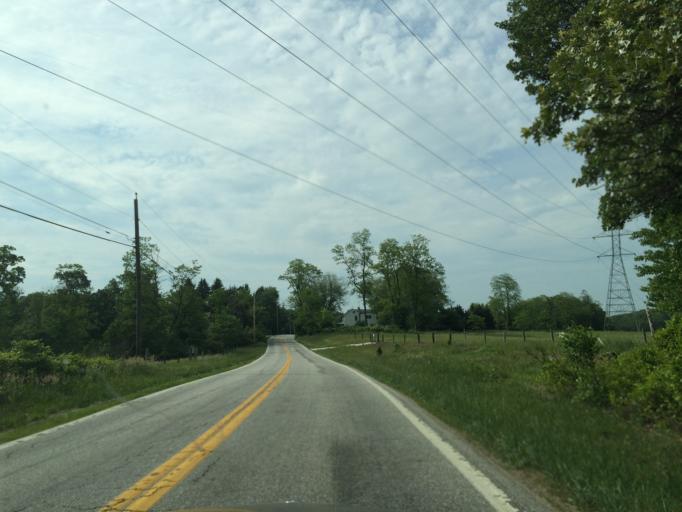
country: US
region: Maryland
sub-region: Baltimore County
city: Reisterstown
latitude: 39.4237
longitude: -76.8406
